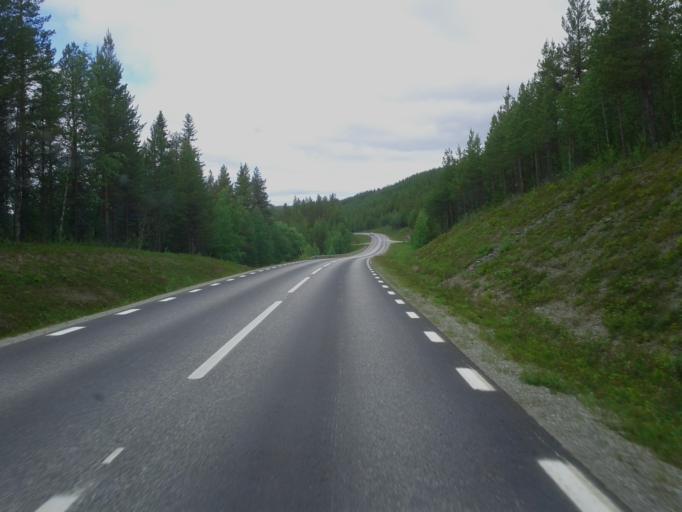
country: SE
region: Vaesterbotten
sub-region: Storumans Kommun
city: Fristad
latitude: 65.3767
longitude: 16.5146
